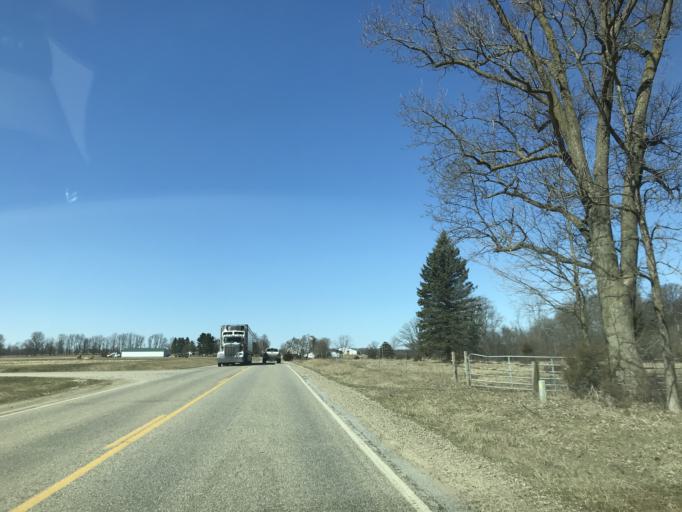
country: US
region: Michigan
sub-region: Hillsdale County
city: Litchfield
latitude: 41.9857
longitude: -84.7921
